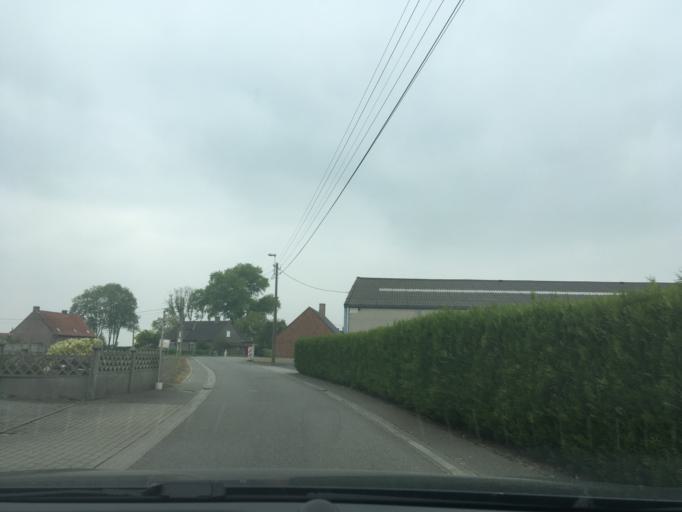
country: BE
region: Flanders
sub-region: Provincie West-Vlaanderen
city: Lichtervelde
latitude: 51.0014
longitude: 3.1332
